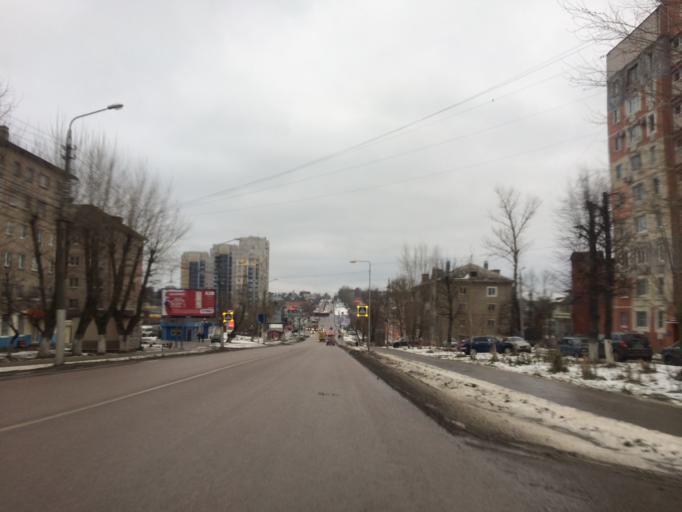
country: RU
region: Tula
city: Tula
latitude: 54.2058
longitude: 37.6758
